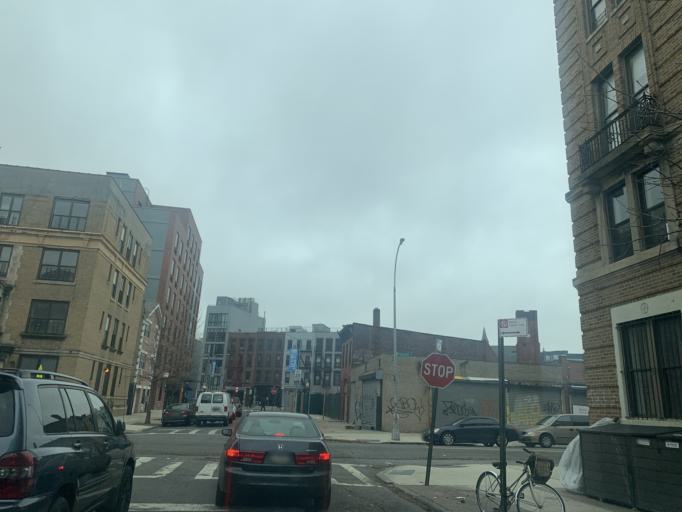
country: US
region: New York
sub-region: Kings County
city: Brooklyn
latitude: 40.6831
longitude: -73.9608
